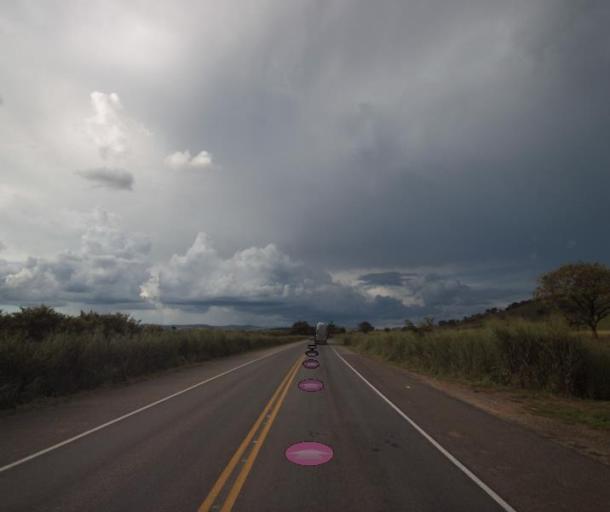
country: BR
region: Goias
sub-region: Ceres
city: Ceres
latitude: -15.2251
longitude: -49.5537
